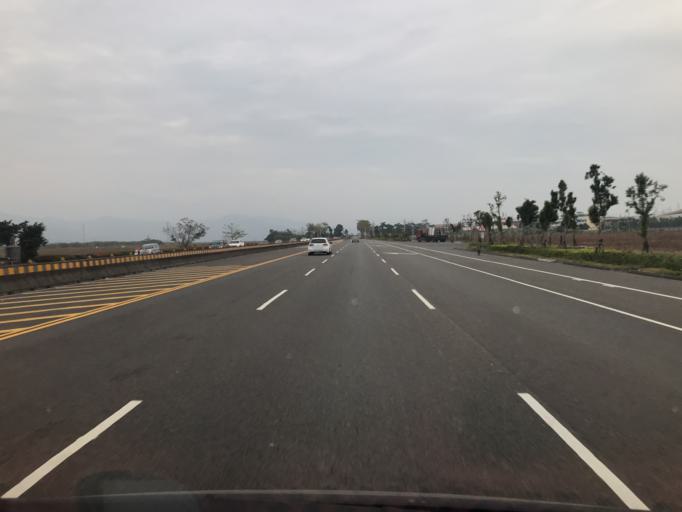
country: TW
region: Taiwan
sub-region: Pingtung
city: Pingtung
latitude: 22.4233
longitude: 120.5801
